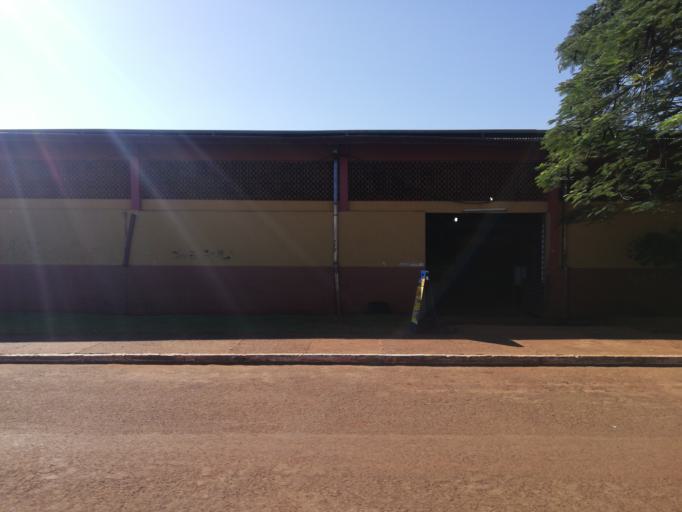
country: PY
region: Alto Parana
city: Presidente Franco
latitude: -25.5259
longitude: -54.6159
